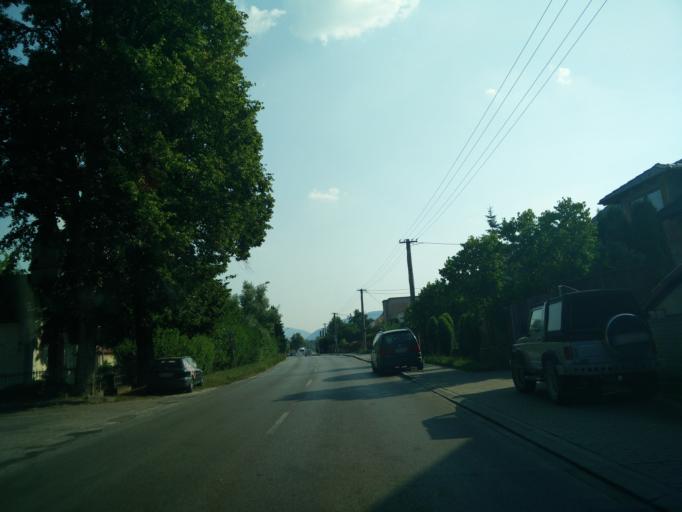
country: SK
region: Zilinsky
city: Rajec
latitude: 49.0832
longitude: 18.6332
